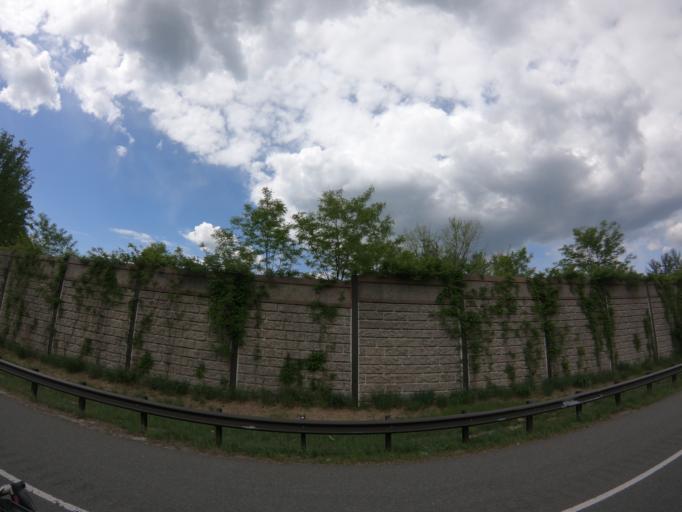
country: US
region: Maryland
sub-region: Montgomery County
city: Fairland
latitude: 39.0834
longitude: -76.9647
